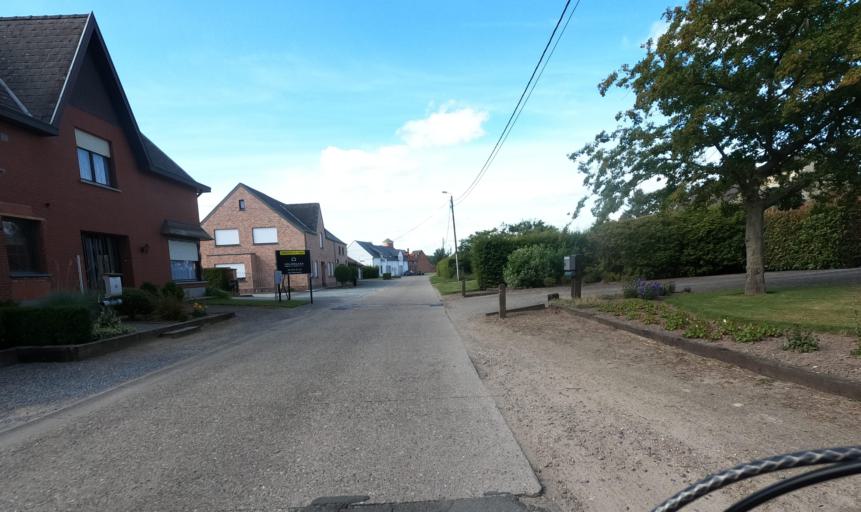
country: BE
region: Flanders
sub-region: Provincie Vlaams-Brabant
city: Kapelle-op-den-Bos
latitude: 51.0282
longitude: 4.4071
